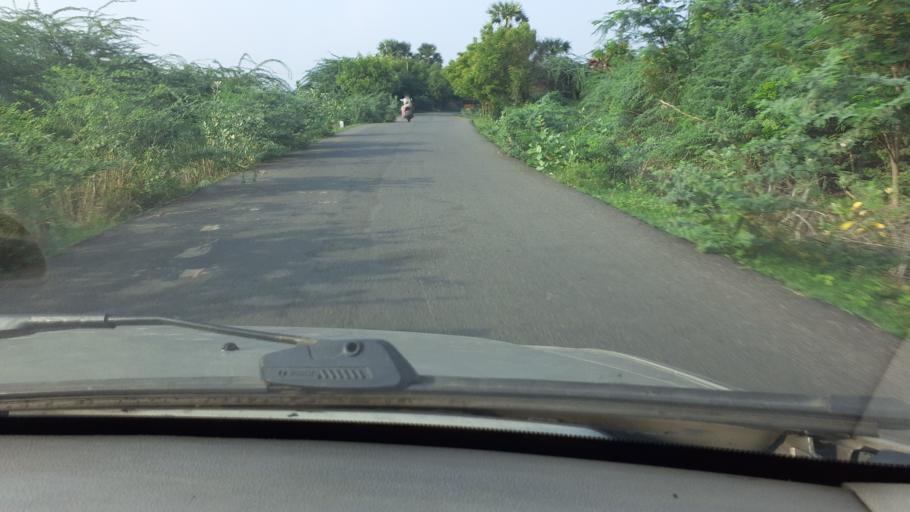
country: IN
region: Tamil Nadu
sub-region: Thoothukkudi
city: Alwar Tirunagari
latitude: 8.5851
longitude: 77.9788
